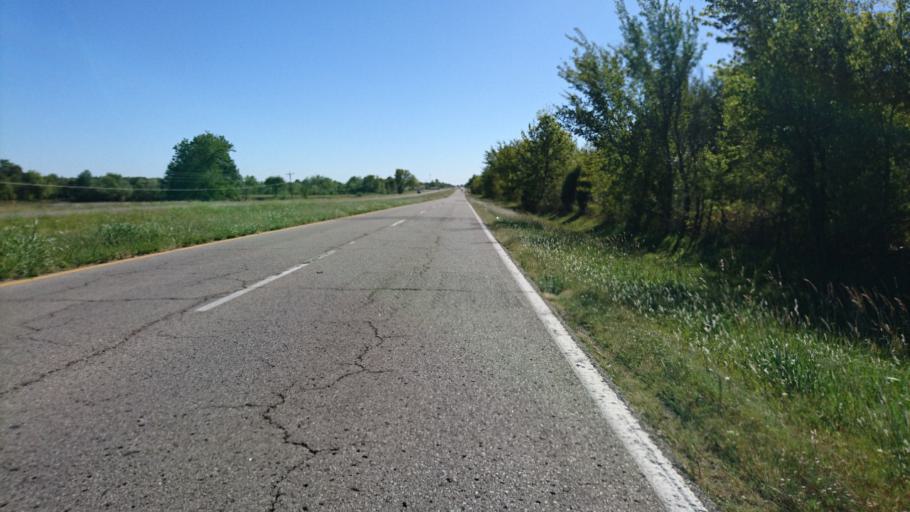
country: US
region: Oklahoma
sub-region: Rogers County
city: Bushyhead
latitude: 36.4007
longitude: -95.5454
